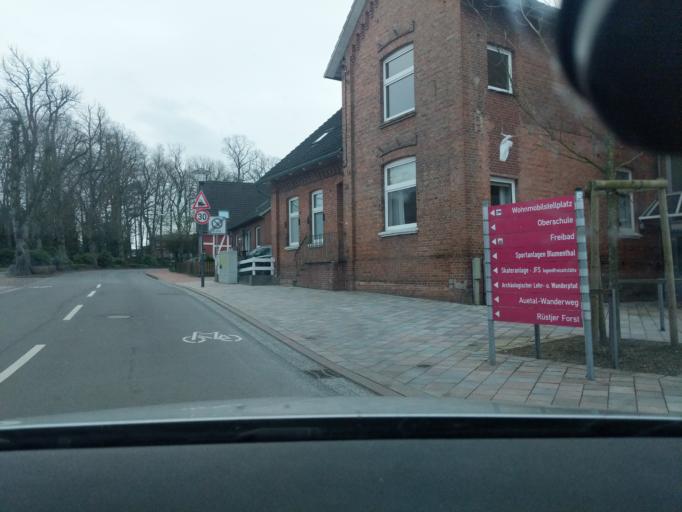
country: DE
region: Lower Saxony
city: Horneburg
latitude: 53.5081
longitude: 9.5794
